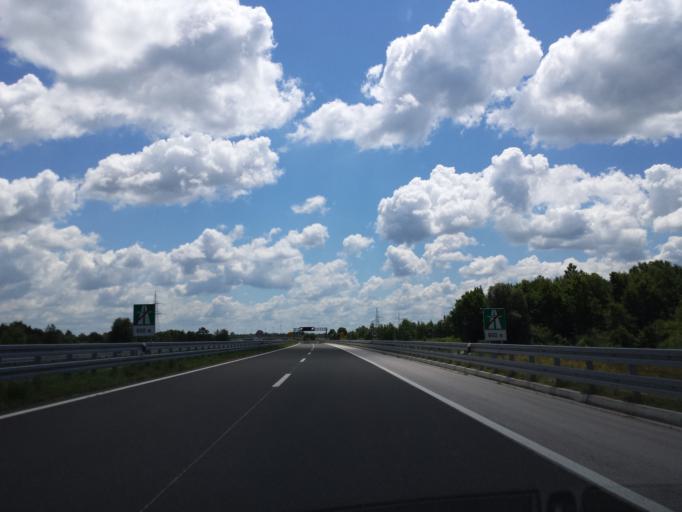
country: HR
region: Sisacko-Moslavacka
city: Lekenik
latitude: 45.5710
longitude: 16.2075
